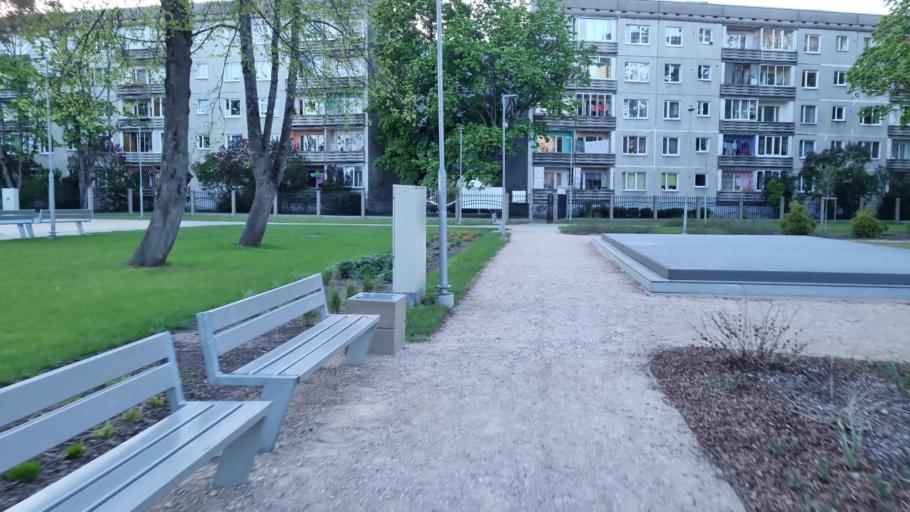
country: LV
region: Marupe
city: Marupe
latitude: 56.9568
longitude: 24.0031
